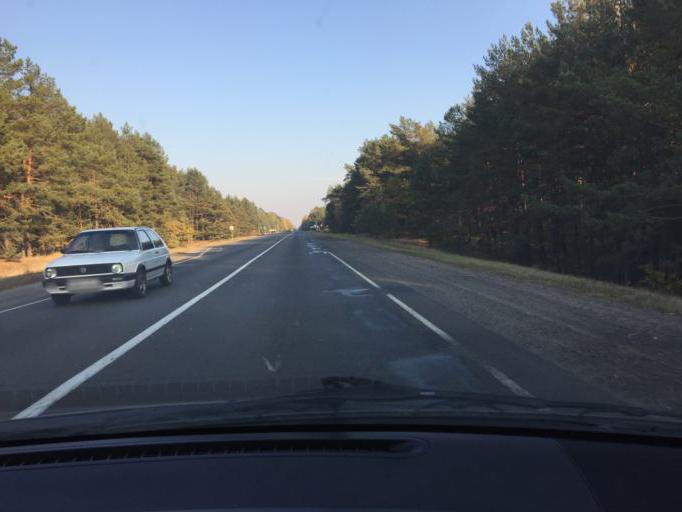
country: BY
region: Brest
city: Davyd-Haradok
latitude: 52.2368
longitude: 27.2607
